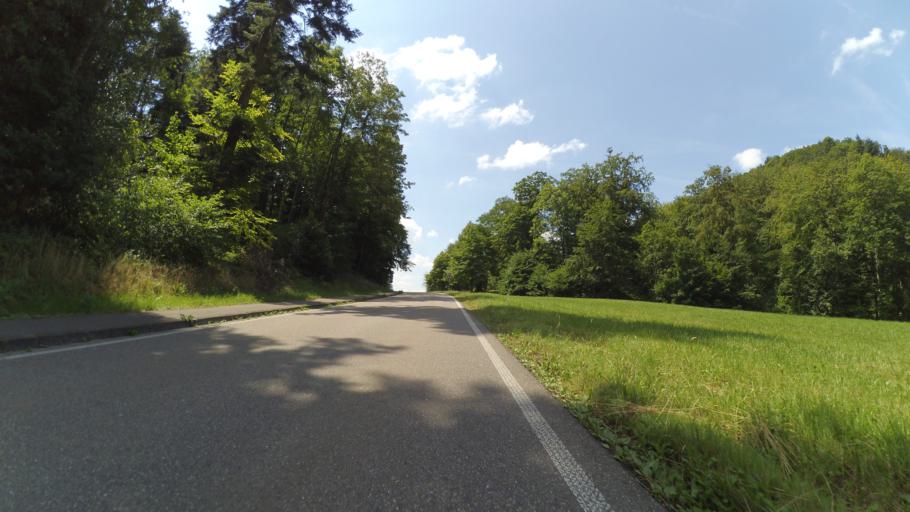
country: DE
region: Baden-Wuerttemberg
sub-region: Freiburg Region
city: Badenweiler
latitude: 47.8159
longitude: 7.6809
